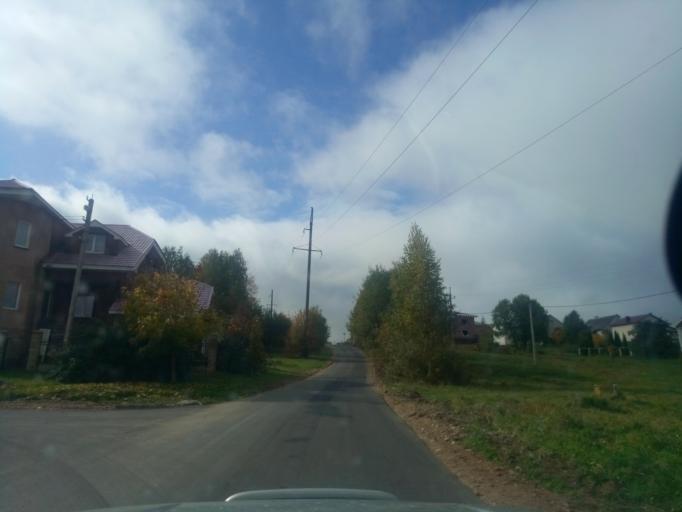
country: BY
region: Minsk
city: Zaslawye
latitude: 54.0016
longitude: 27.2688
